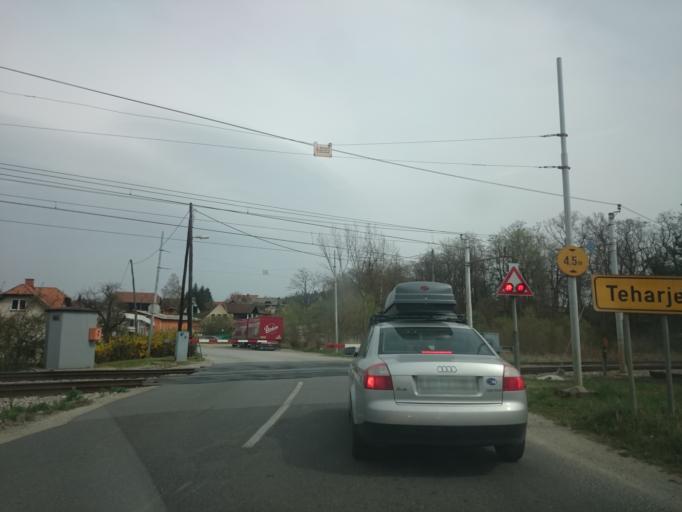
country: SI
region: Store
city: Store
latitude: 46.2296
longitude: 15.2969
